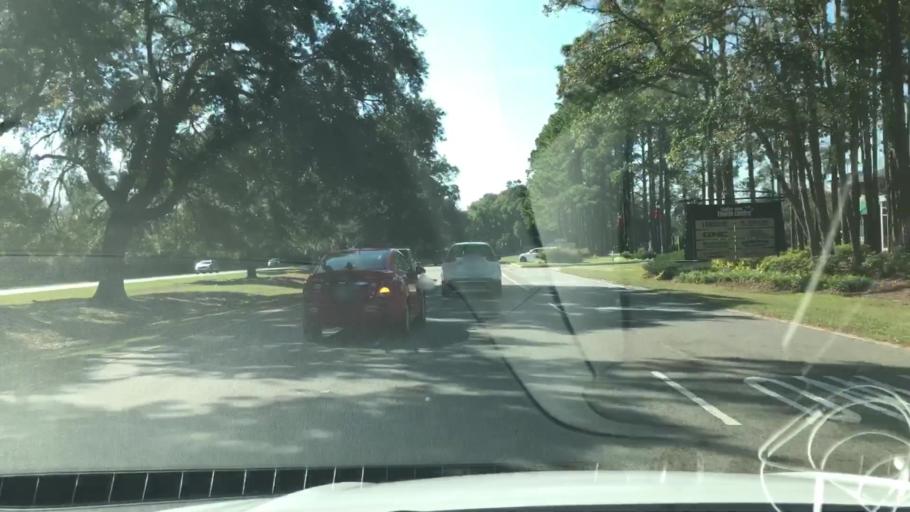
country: US
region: South Carolina
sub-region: Beaufort County
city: Hilton Head Island
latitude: 32.1845
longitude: -80.7192
